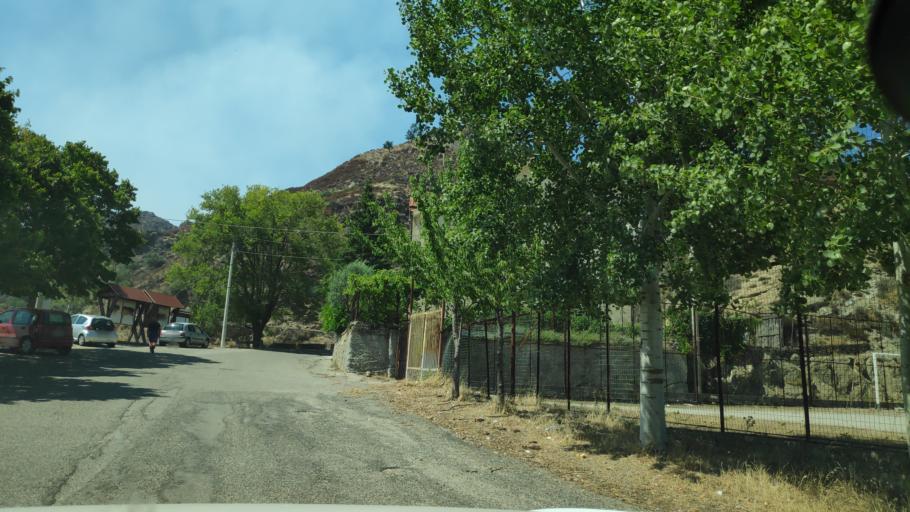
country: IT
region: Calabria
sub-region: Provincia di Reggio Calabria
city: Bova
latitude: 37.9987
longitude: 15.9309
